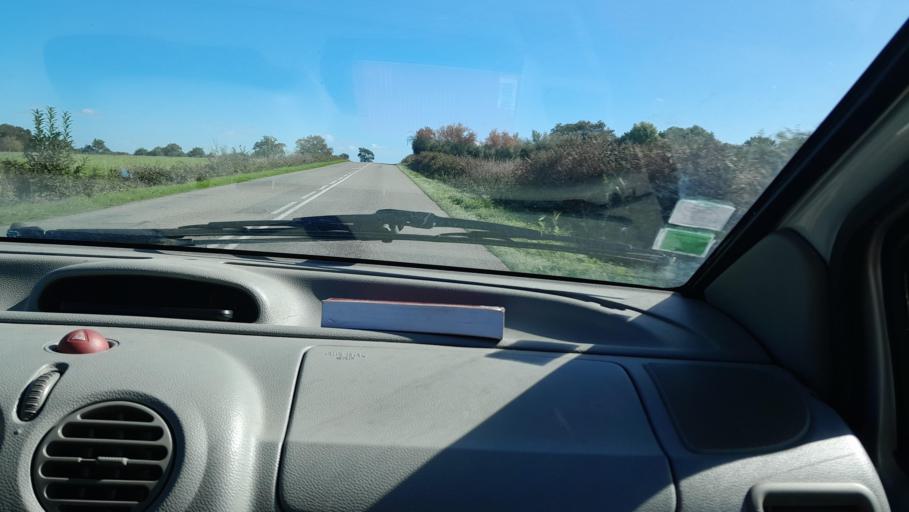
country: FR
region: Pays de la Loire
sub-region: Departement de la Mayenne
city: Quelaines-Saint-Gault
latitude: 47.9346
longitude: -0.8500
